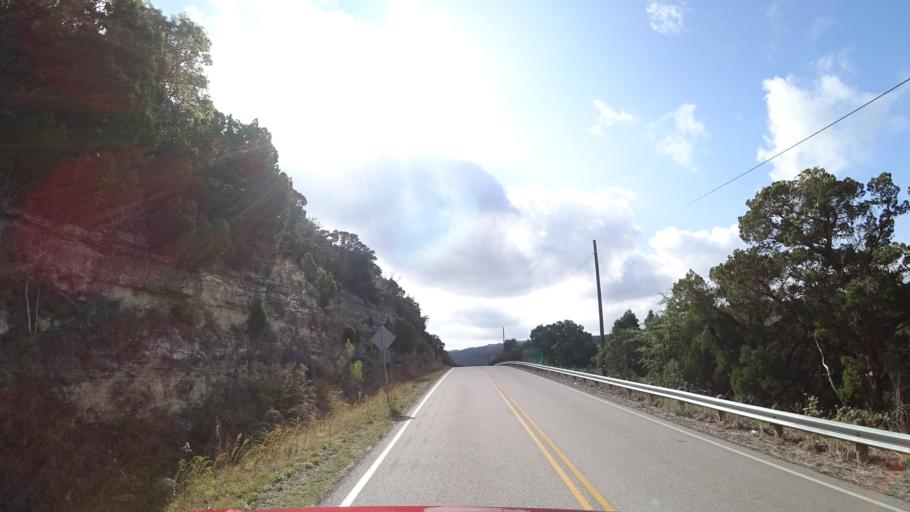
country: US
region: Texas
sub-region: Travis County
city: Hudson Bend
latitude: 30.4276
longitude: -97.8727
